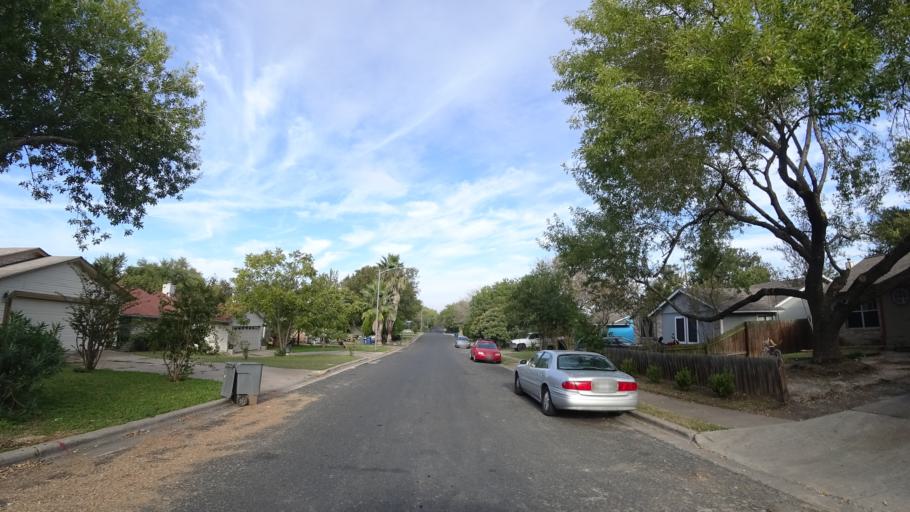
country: US
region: Texas
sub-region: Travis County
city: Austin
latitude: 30.1955
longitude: -97.7293
